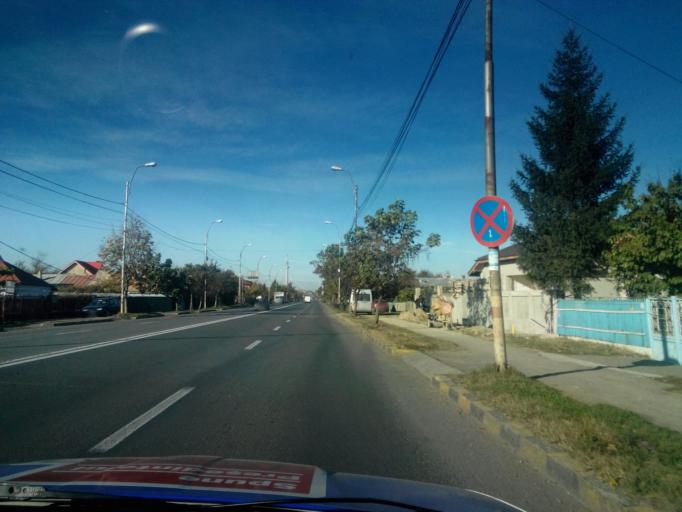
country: RO
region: Bacau
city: Margineni-Munteni
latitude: 46.5860
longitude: 26.9303
